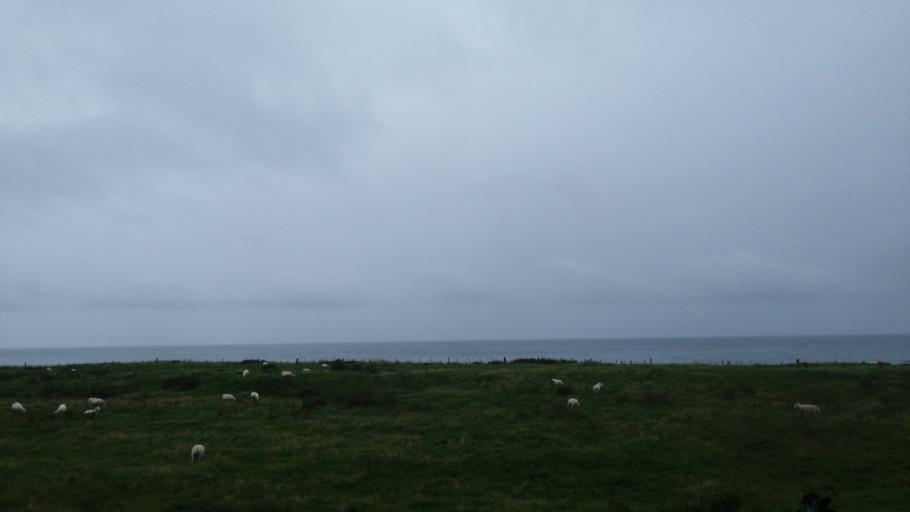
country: GB
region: Scotland
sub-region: Highland
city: Brora
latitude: 58.0454
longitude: -3.8189
